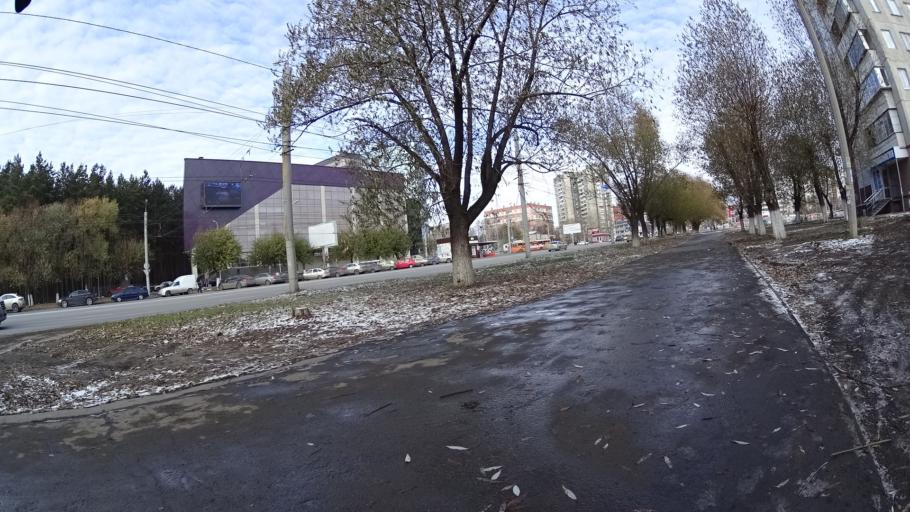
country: RU
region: Chelyabinsk
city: Roshchino
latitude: 55.1923
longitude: 61.2990
